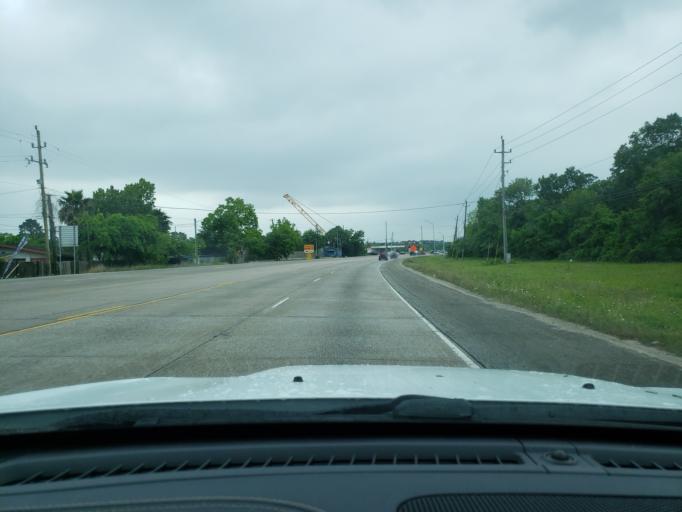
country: US
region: Texas
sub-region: Harris County
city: Baytown
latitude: 29.7753
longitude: -94.9137
